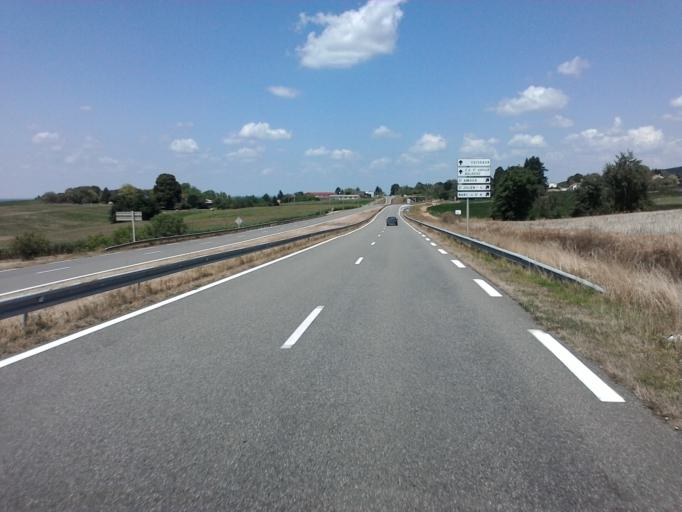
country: FR
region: Franche-Comte
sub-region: Departement du Jura
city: Saint-Amour
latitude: 46.4182
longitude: 5.3511
